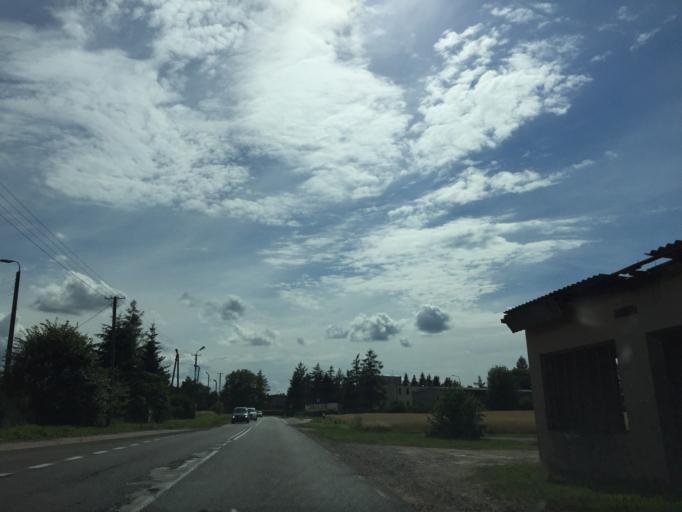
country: PL
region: Masovian Voivodeship
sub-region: Powiat losicki
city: Losice
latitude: 52.2431
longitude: 22.7773
